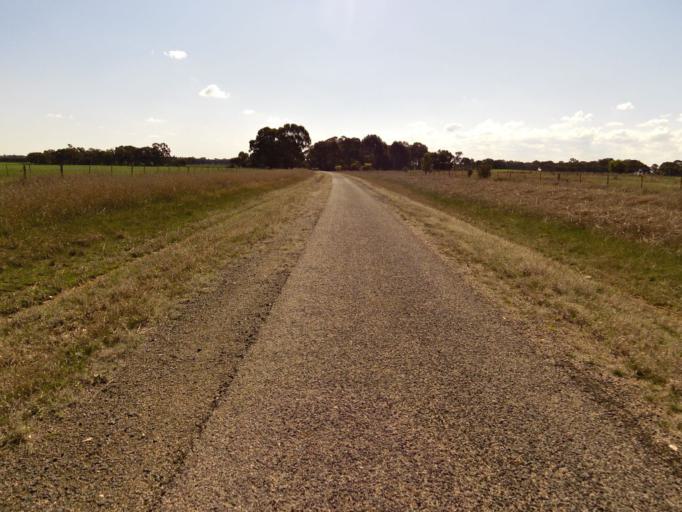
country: AU
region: New South Wales
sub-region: Corowa Shire
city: Corowa
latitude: -36.0392
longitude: 146.4531
